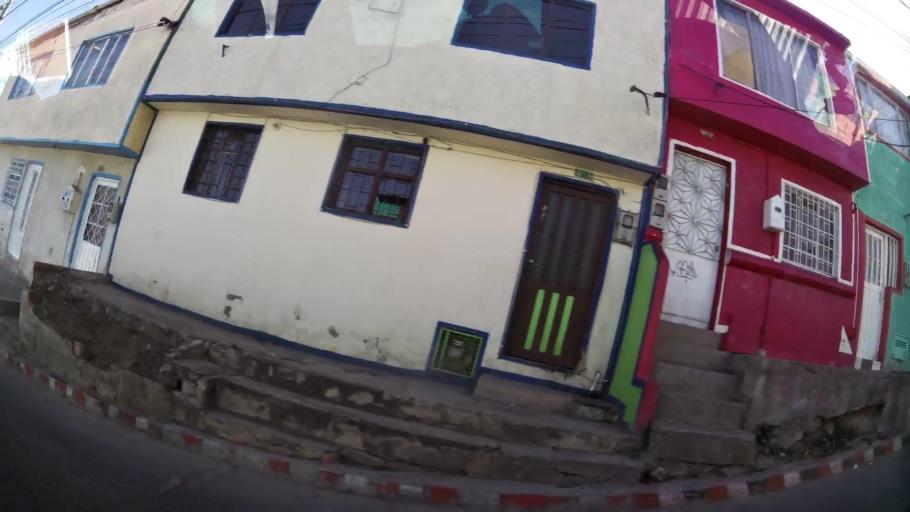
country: CO
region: Cundinamarca
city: Soacha
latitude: 4.5541
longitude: -74.1441
